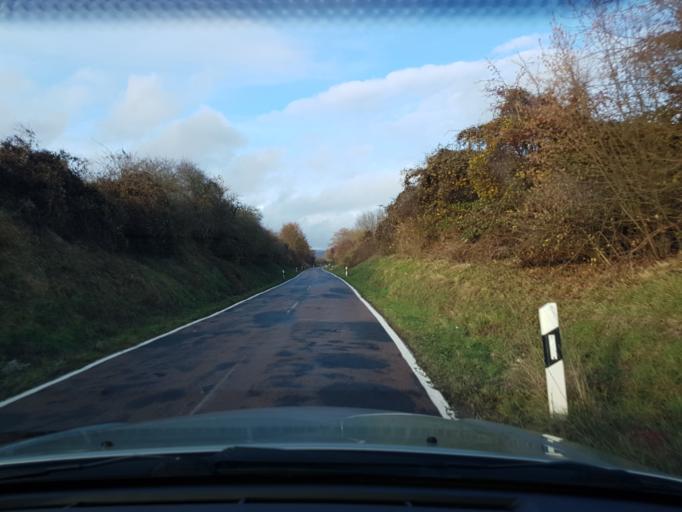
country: DE
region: Hesse
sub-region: Regierungsbezirk Darmstadt
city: Kiedrich
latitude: 50.0202
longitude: 8.0607
